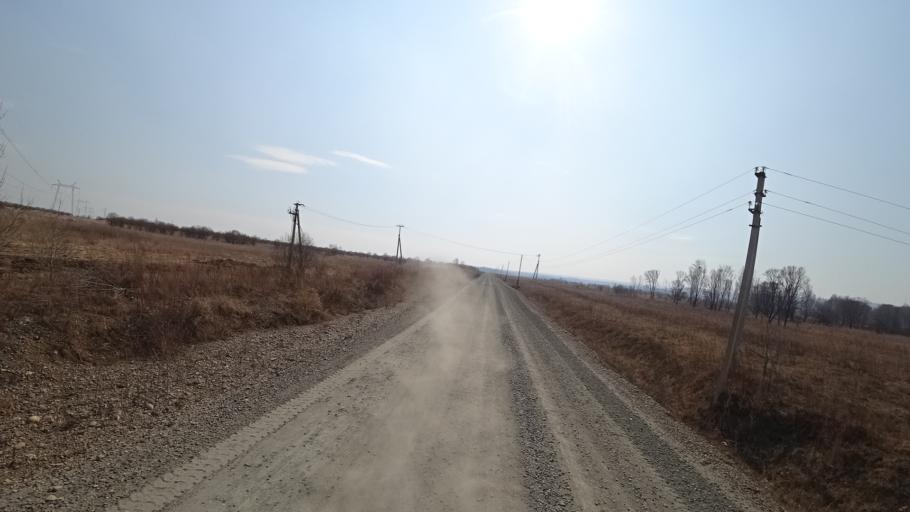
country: RU
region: Amur
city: Novobureyskiy
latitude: 49.8146
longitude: 129.9744
